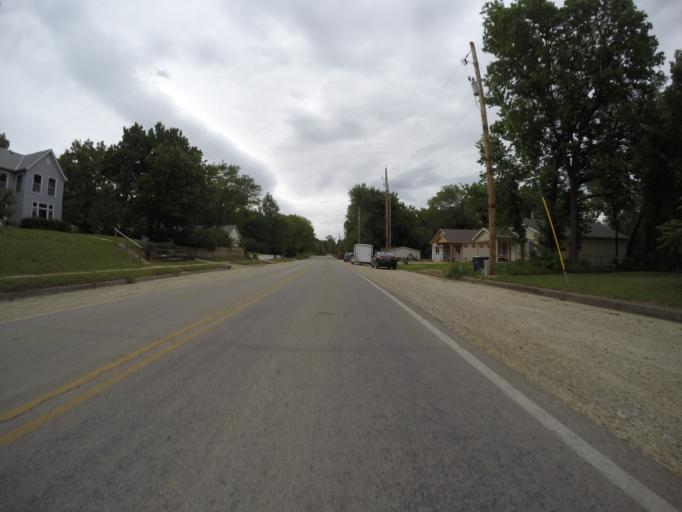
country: US
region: Kansas
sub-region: Pottawatomie County
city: Wamego
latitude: 39.1896
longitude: -96.4185
